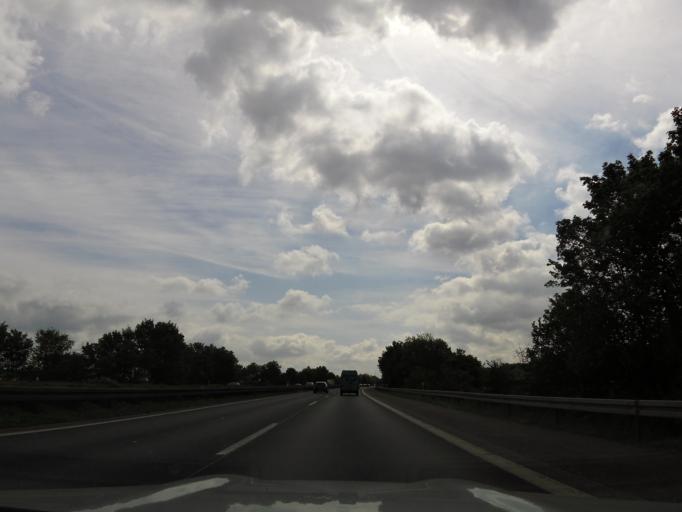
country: DE
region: Hesse
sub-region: Regierungsbezirk Giessen
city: Langgons
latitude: 50.5163
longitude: 8.6671
